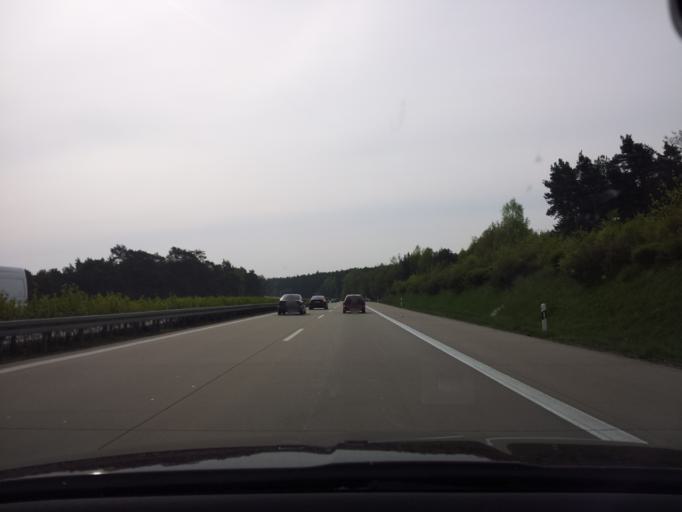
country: DE
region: Brandenburg
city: Luebben
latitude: 51.8981
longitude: 13.8150
